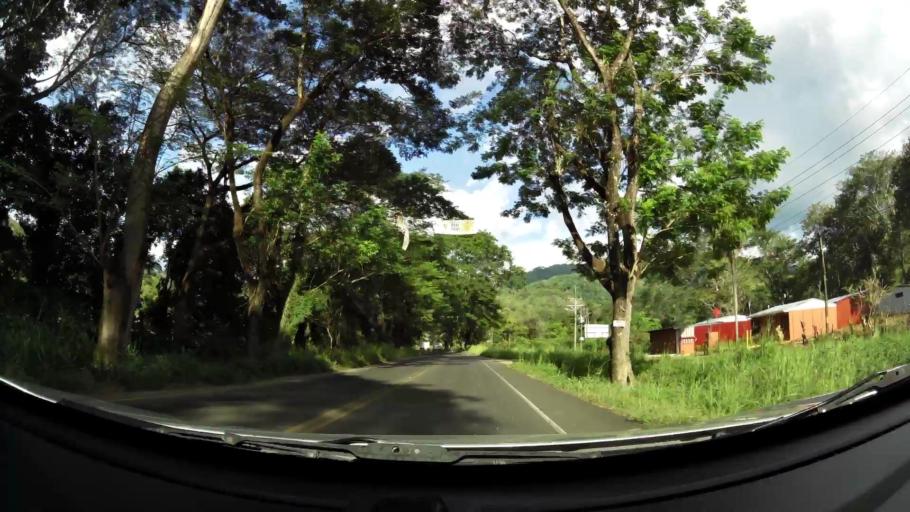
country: CR
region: Puntarenas
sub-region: Canton de Garabito
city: Jaco
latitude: 9.7218
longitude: -84.6298
